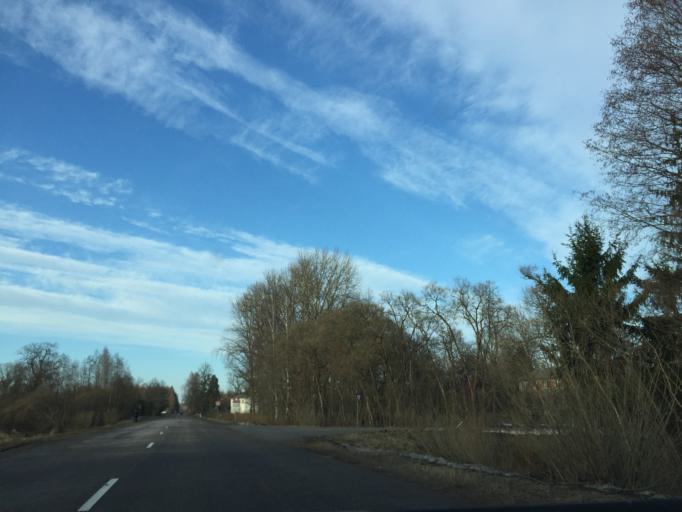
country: LV
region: Kekava
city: Balozi
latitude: 56.7337
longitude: 24.1095
